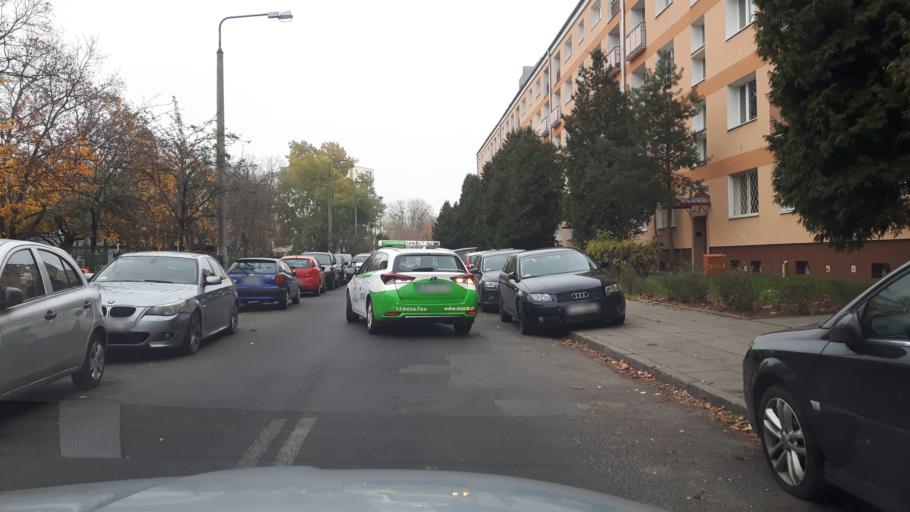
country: PL
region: Masovian Voivodeship
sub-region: Warszawa
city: Praga Polnoc
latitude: 52.2651
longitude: 21.0292
